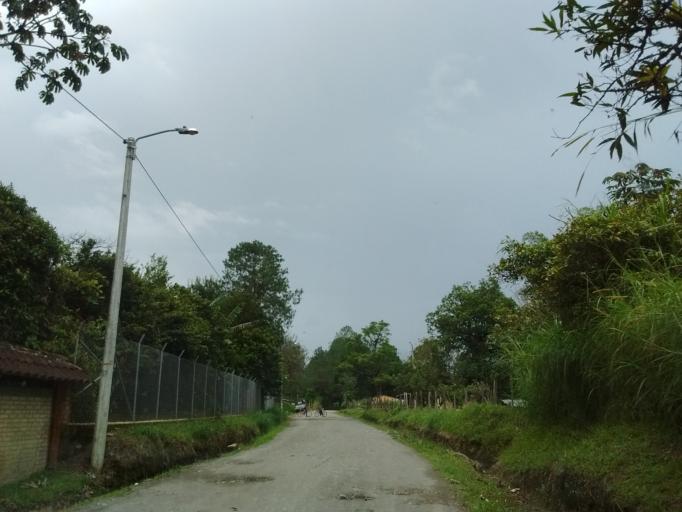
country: CO
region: Cauca
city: Cajibio
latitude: 2.5465
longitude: -76.6238
